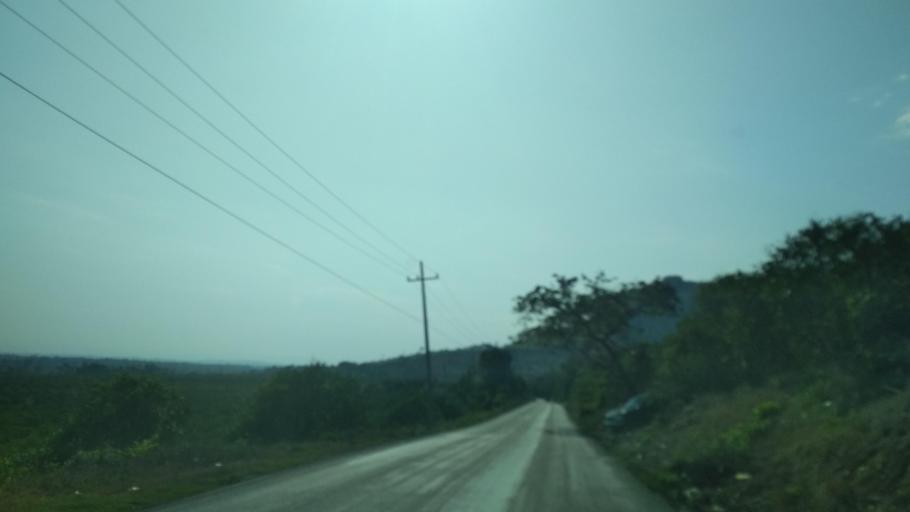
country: MX
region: Veracruz
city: Agua Dulce
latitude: 20.3945
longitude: -97.2743
